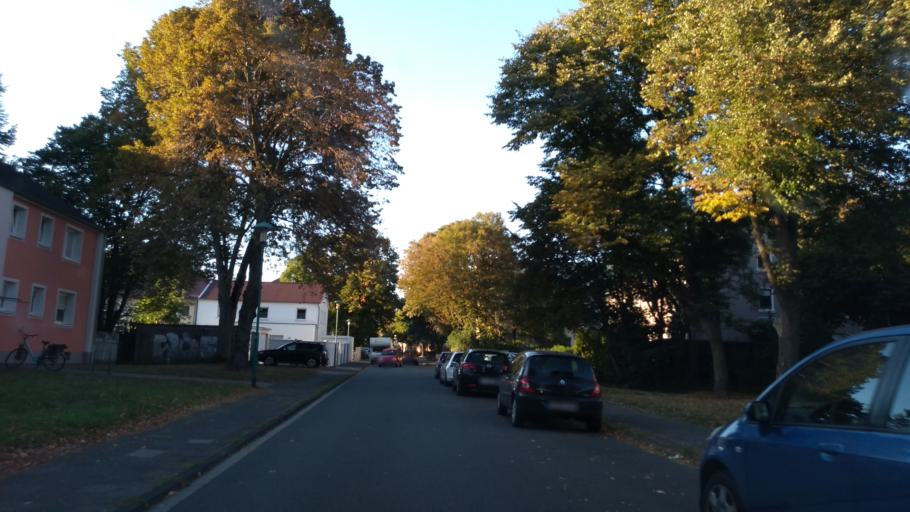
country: DE
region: North Rhine-Westphalia
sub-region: Regierungsbezirk Dusseldorf
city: Dinslaken
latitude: 51.5487
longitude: 6.7185
